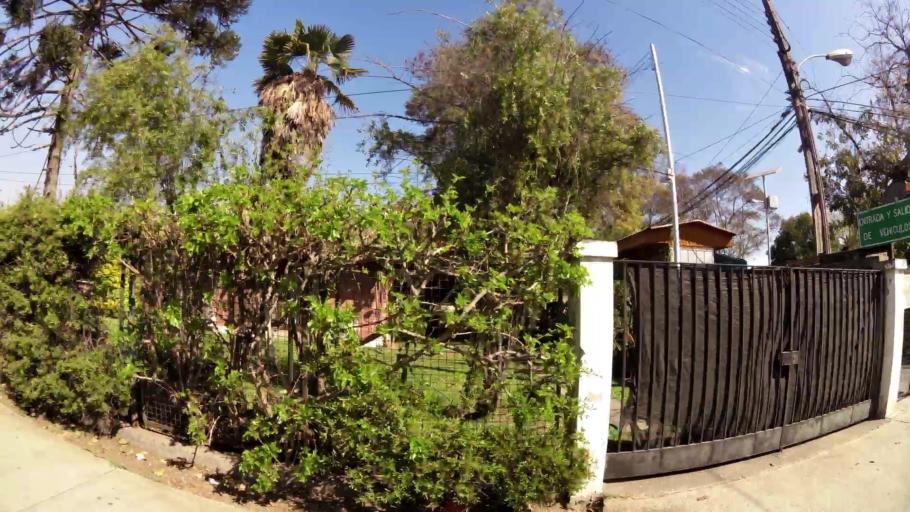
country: CL
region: Santiago Metropolitan
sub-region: Provincia de Santiago
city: Villa Presidente Frei, Nunoa, Santiago, Chile
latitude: -33.5208
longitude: -70.6065
